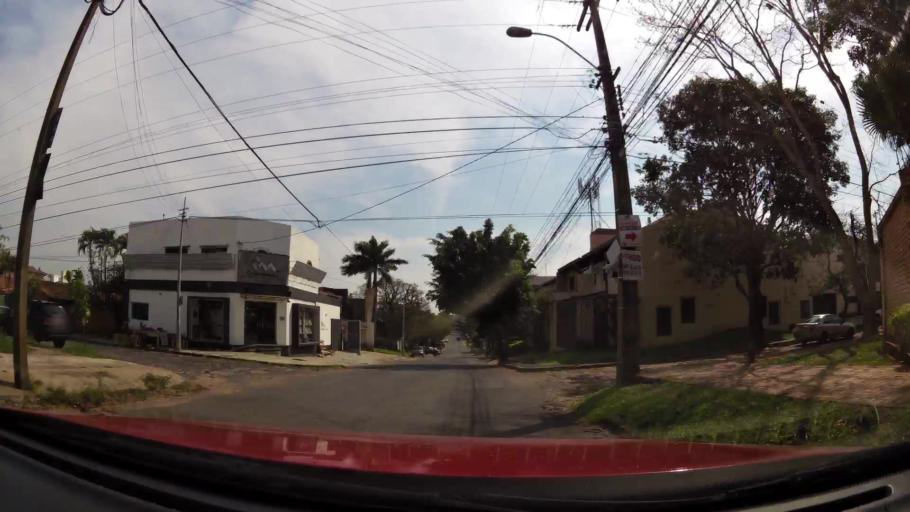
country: PY
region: Asuncion
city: Asuncion
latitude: -25.2667
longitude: -57.5613
